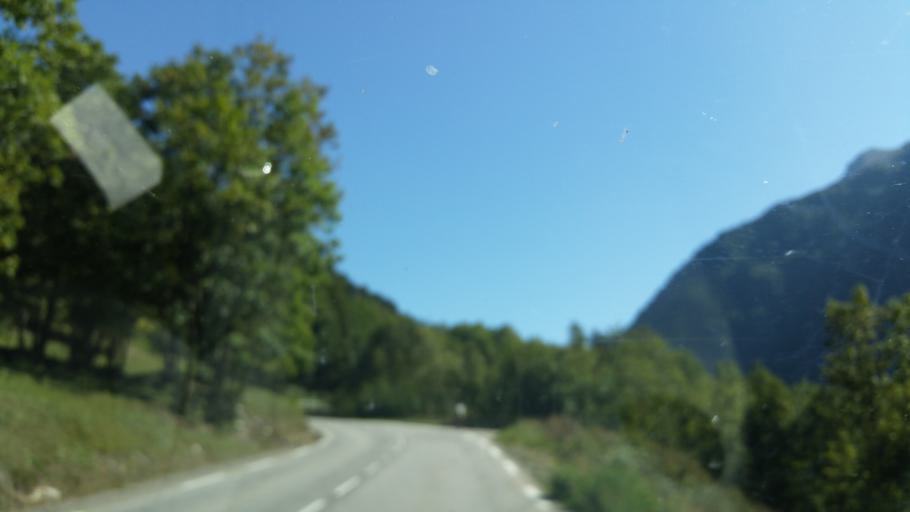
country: FR
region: Rhone-Alpes
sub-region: Departement de la Savoie
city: Tignes
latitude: 45.5770
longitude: 6.8831
